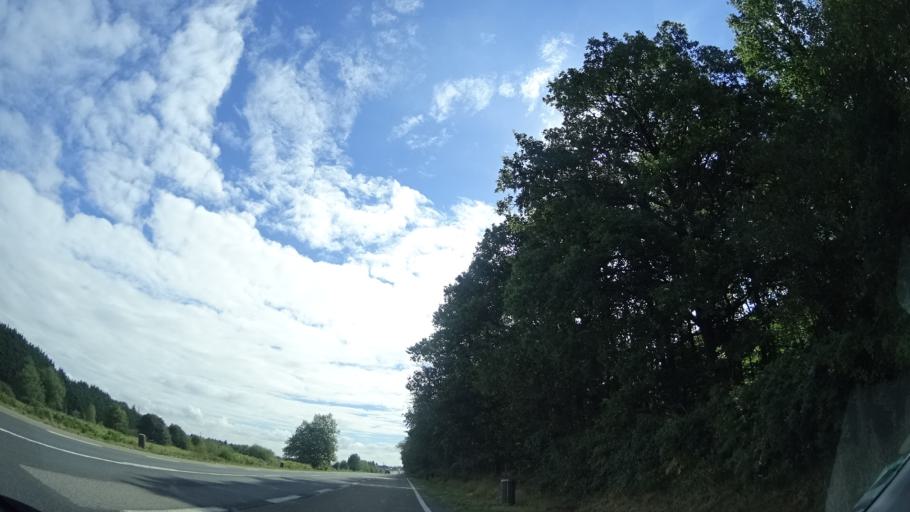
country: FR
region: Pays de la Loire
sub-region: Departement de la Mayenne
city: Port-Brillet
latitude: 48.0752
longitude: -0.9819
